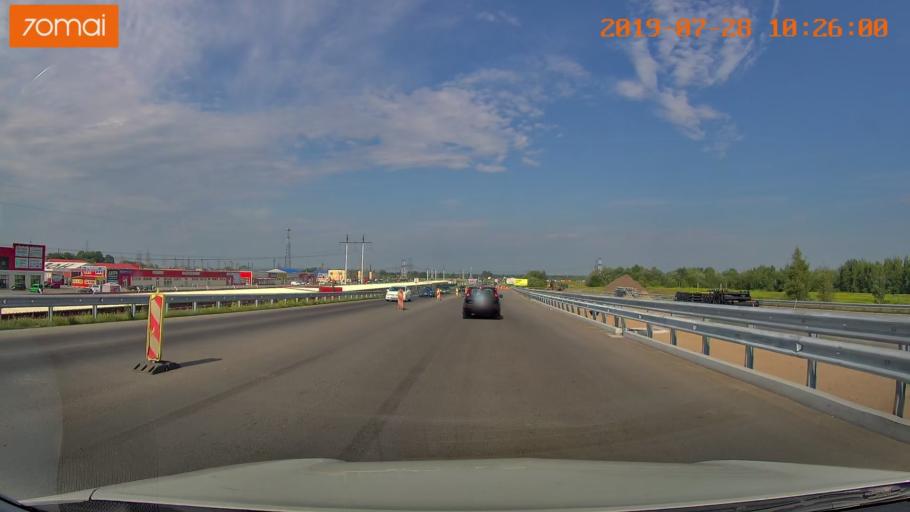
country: RU
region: Kaliningrad
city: Maloye Isakovo
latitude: 54.7682
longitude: 20.5337
